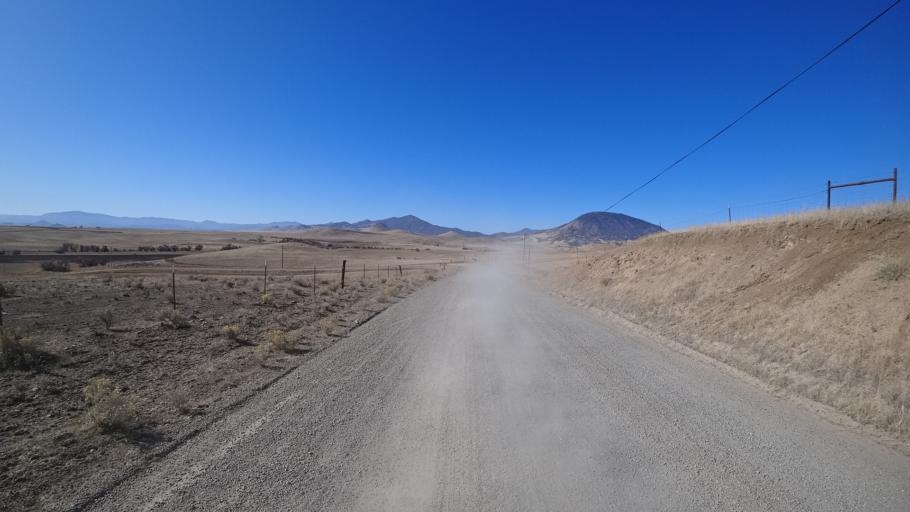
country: US
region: California
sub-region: Siskiyou County
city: Montague
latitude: 41.8298
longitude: -122.4188
